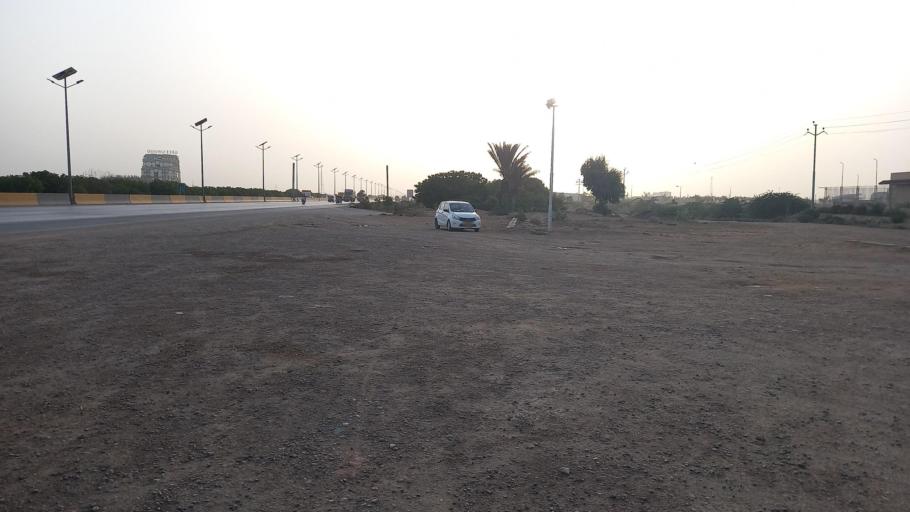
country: PK
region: Sindh
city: Malir Cantonment
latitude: 24.9904
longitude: 67.1778
